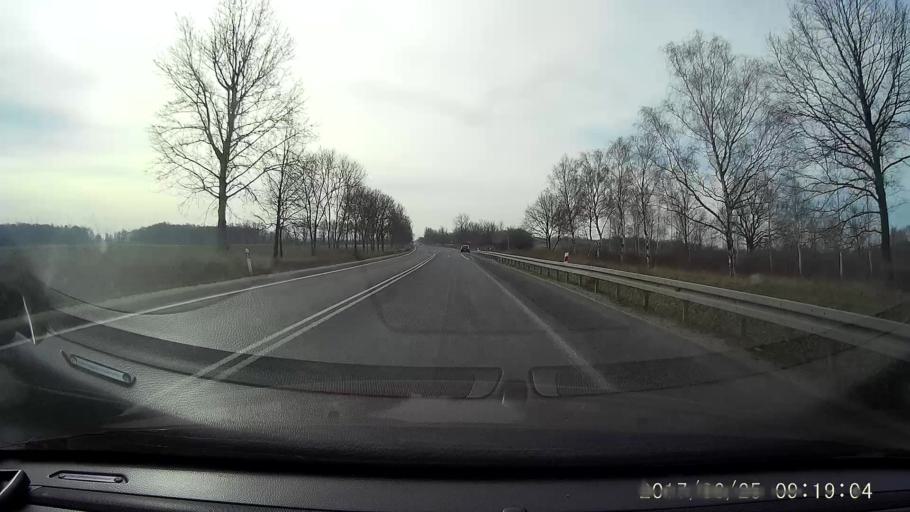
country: PL
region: Lower Silesian Voivodeship
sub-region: Powiat zgorzelecki
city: Zgorzelec
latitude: 51.1120
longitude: 15.0137
